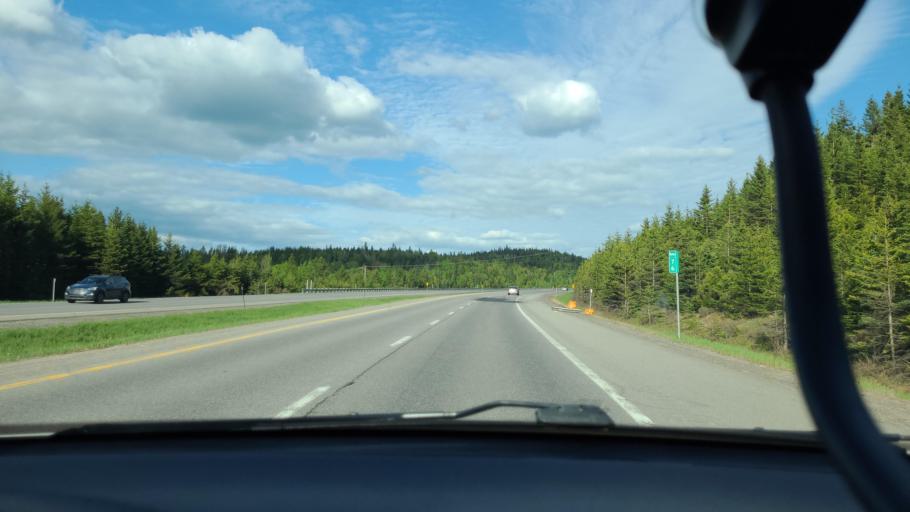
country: CA
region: Quebec
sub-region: Laurentides
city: Val-David
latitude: 45.9900
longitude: -74.2012
